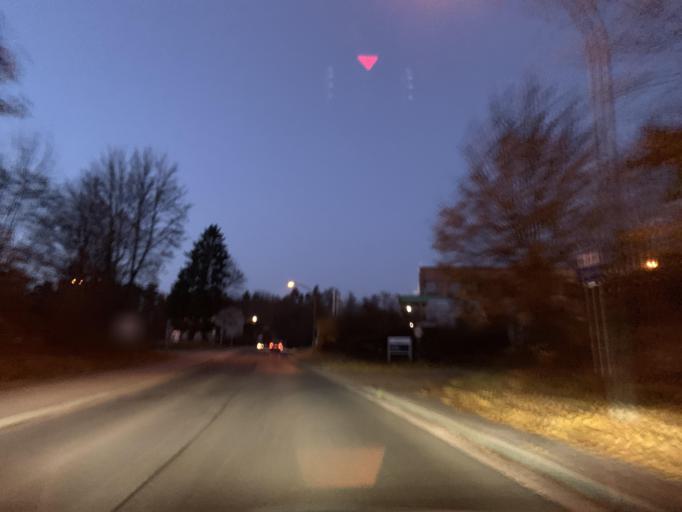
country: DE
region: Bavaria
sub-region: Upper Palatinate
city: Bodenwohr
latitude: 49.2771
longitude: 12.3299
